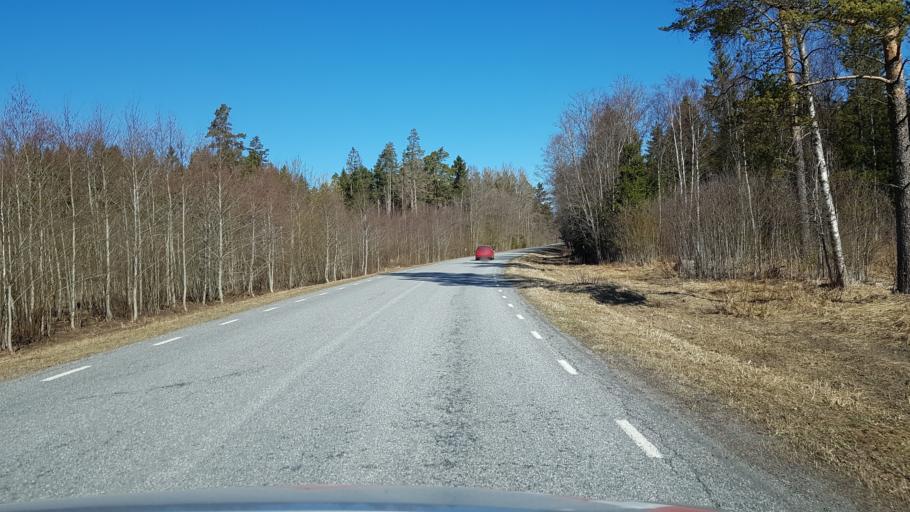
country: EE
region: Laeaene-Virumaa
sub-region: Haljala vald
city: Haljala
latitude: 59.4799
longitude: 26.2478
